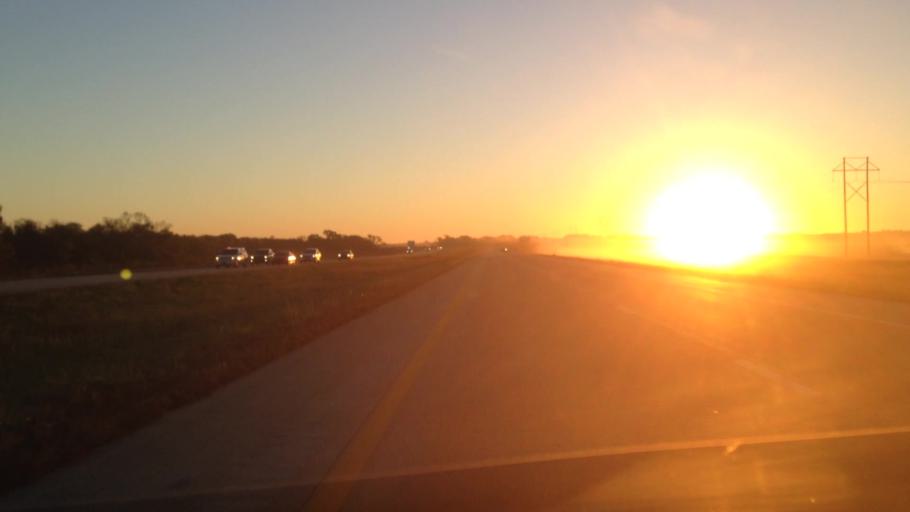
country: US
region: Kansas
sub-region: Douglas County
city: Lawrence
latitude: 38.9227
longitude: -95.1989
